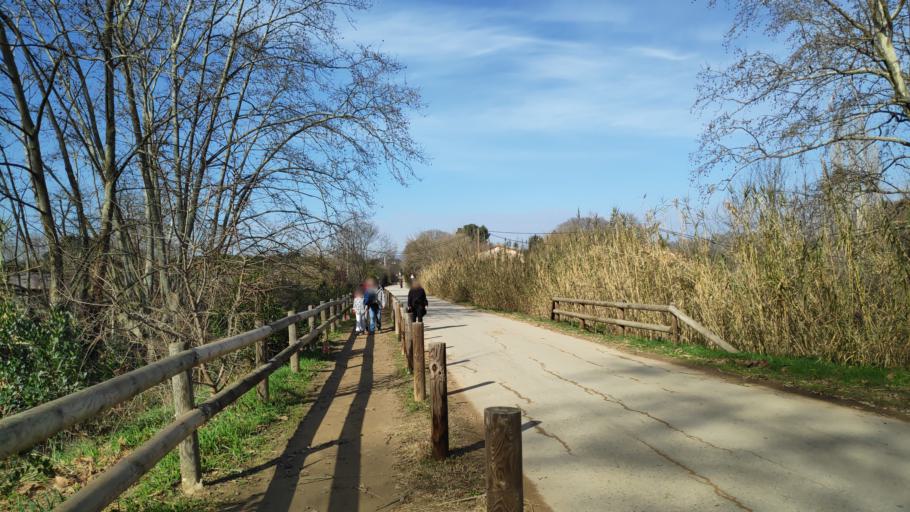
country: ES
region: Catalonia
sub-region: Provincia de Barcelona
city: Mollet del Valles
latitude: 41.5631
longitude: 2.1969
